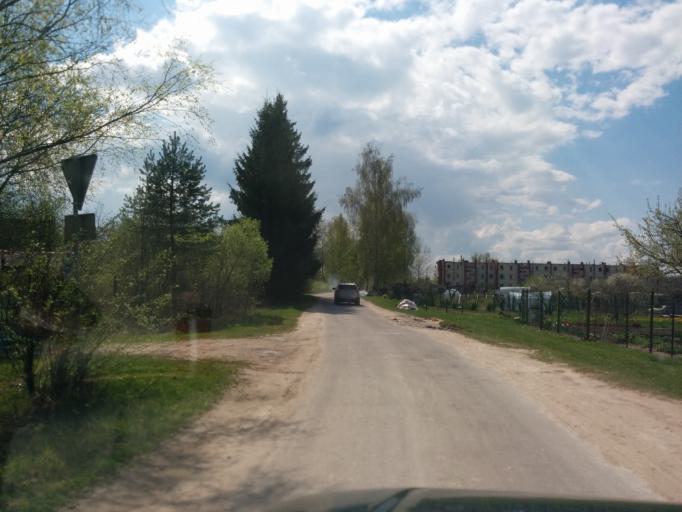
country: LV
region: Ozolnieku
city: Ozolnieki
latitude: 56.6353
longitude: 23.7906
